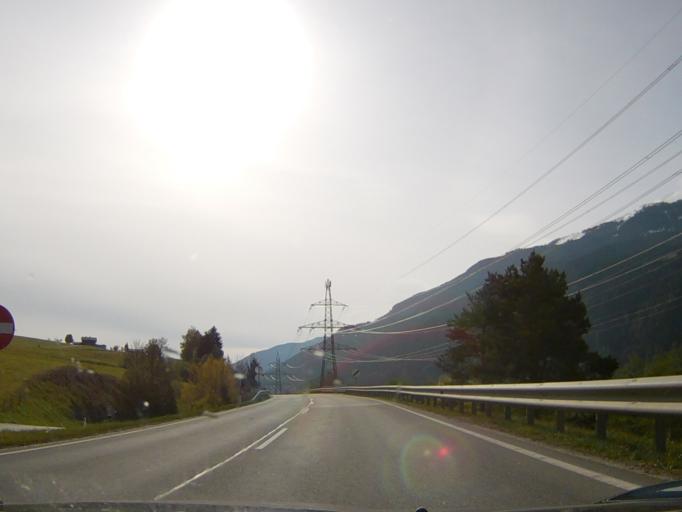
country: AT
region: Salzburg
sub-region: Politischer Bezirk Zell am See
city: Hollersbach im Pinzgau
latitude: 47.2817
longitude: 12.4057
